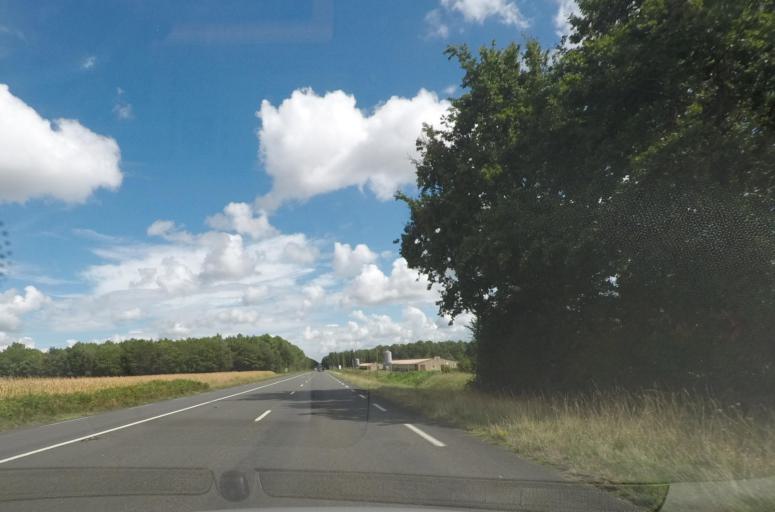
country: FR
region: Pays de la Loire
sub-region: Departement de la Sarthe
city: Mezeray
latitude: 47.7755
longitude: 0.0280
